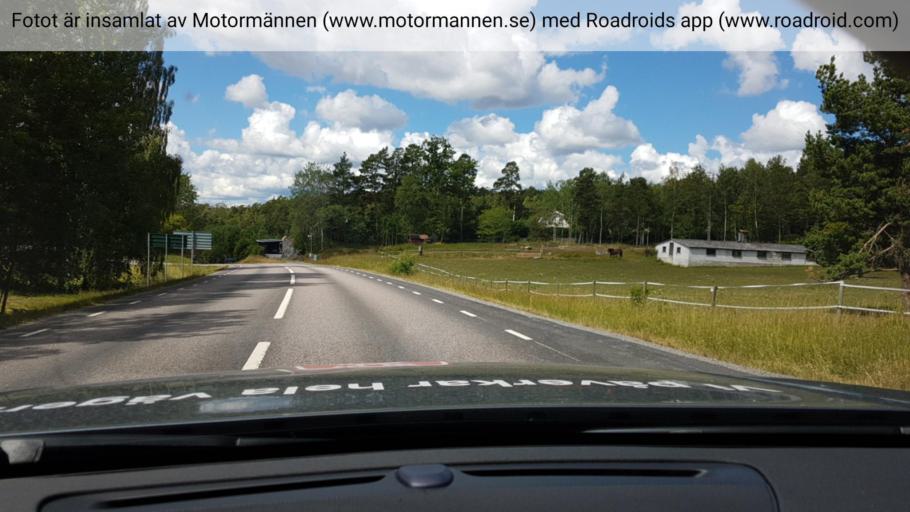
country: SE
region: Stockholm
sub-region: Varmdo Kommun
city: Mortnas
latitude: 59.3968
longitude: 18.4566
